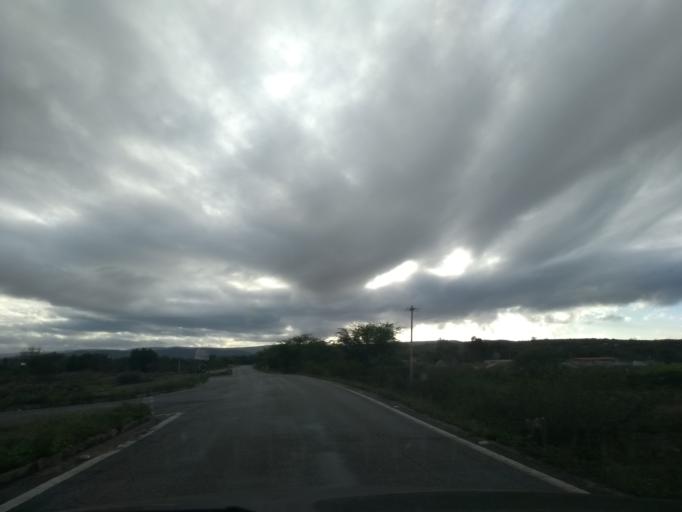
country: BR
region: Bahia
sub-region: Ituacu
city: Ituacu
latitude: -13.7695
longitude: -41.0445
